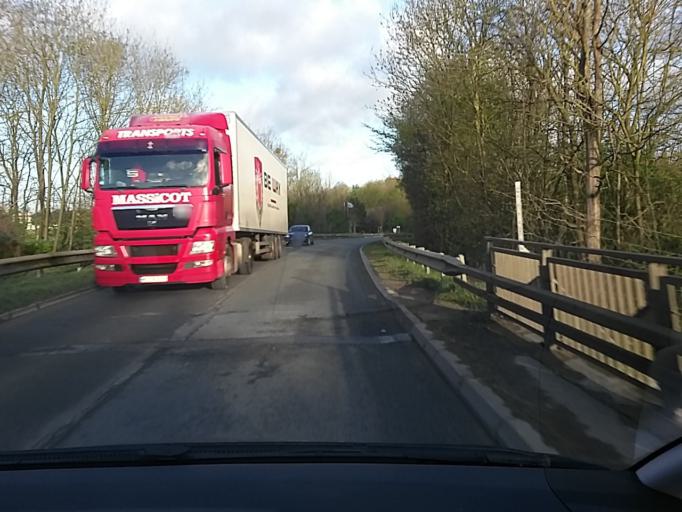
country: FR
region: Picardie
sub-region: Departement de l'Oise
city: Chevrieres
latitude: 49.3265
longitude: 2.6901
